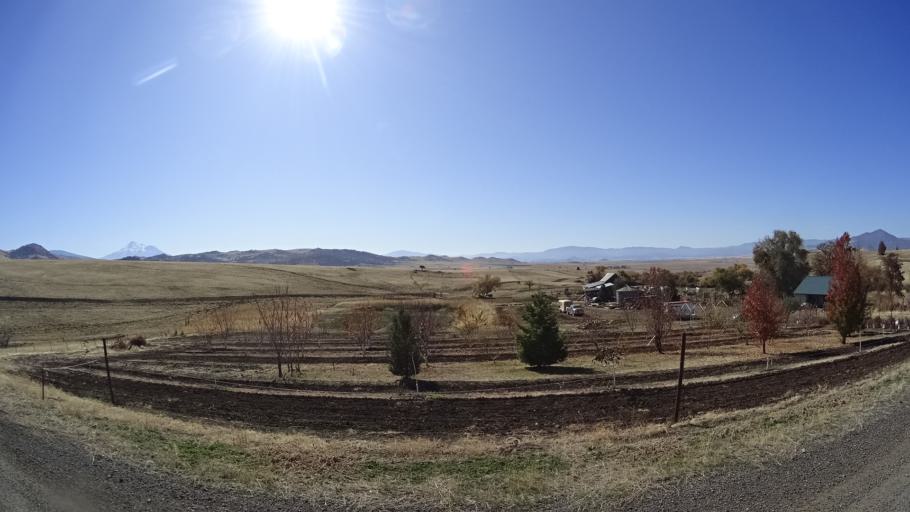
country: US
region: California
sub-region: Siskiyou County
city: Montague
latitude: 41.8311
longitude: -122.3871
